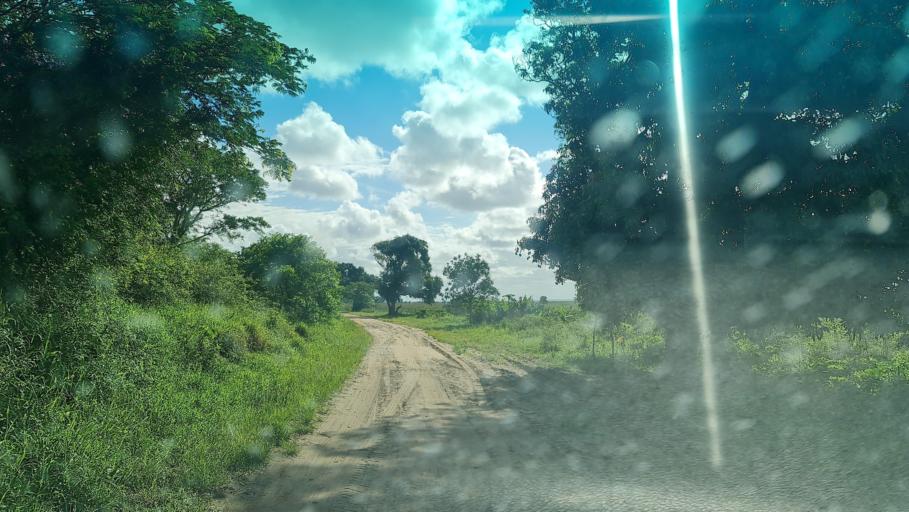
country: MZ
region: Maputo
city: Manhica
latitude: -25.4286
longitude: 32.8950
